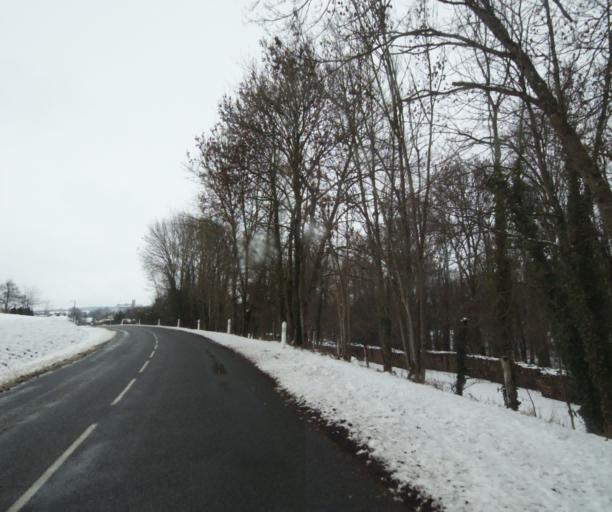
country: FR
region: Champagne-Ardenne
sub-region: Departement de la Haute-Marne
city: Wassy
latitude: 48.4416
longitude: 4.9556
